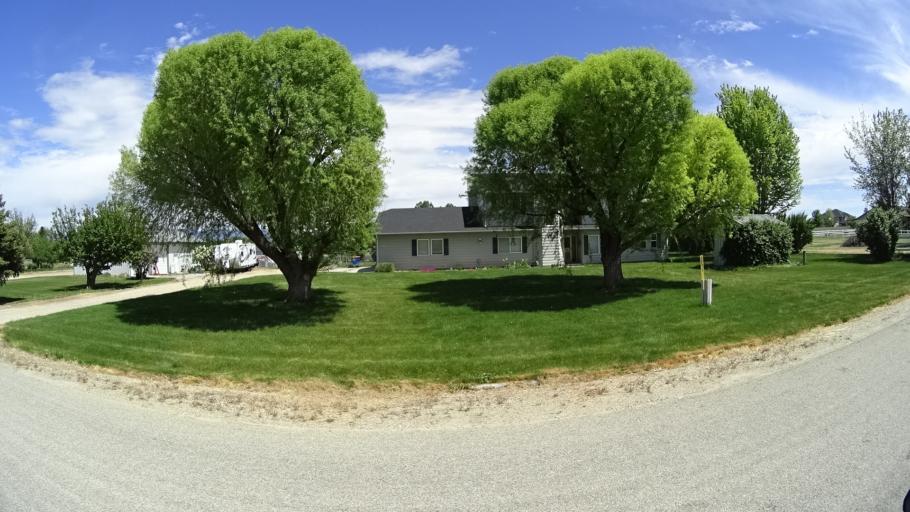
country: US
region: Idaho
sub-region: Ada County
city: Meridian
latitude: 43.5733
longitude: -116.3464
